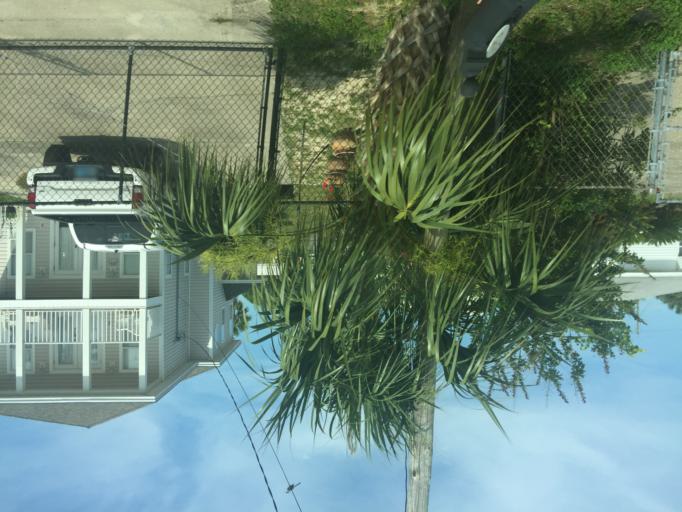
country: US
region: Florida
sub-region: Bay County
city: Laguna Beach
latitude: 30.2482
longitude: -85.9348
